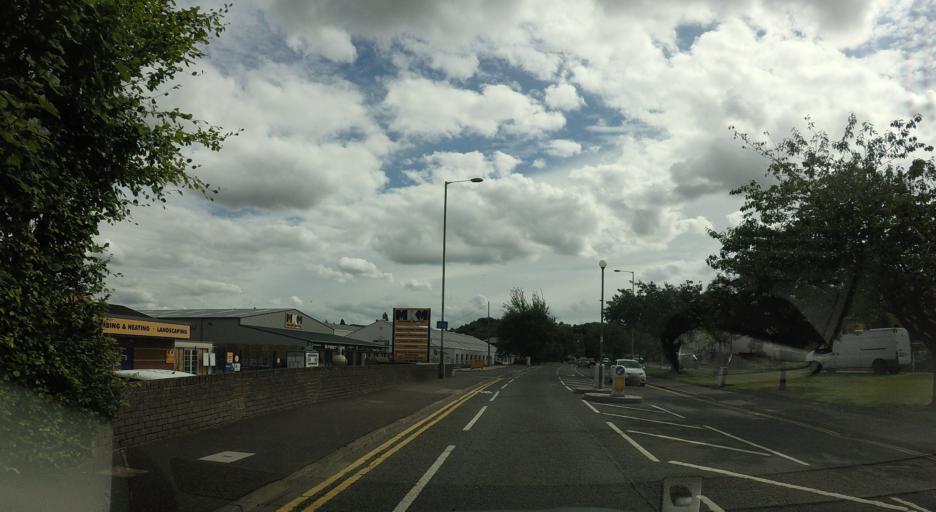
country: GB
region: Scotland
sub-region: Perth and Kinross
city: Perth
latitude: 56.3847
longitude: -3.4366
